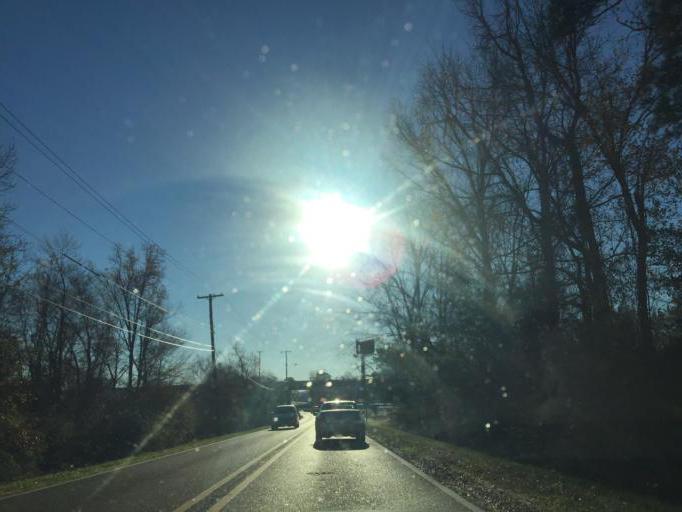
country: US
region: Mississippi
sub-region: Hinds County
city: Jackson
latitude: 32.2847
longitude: -90.1734
